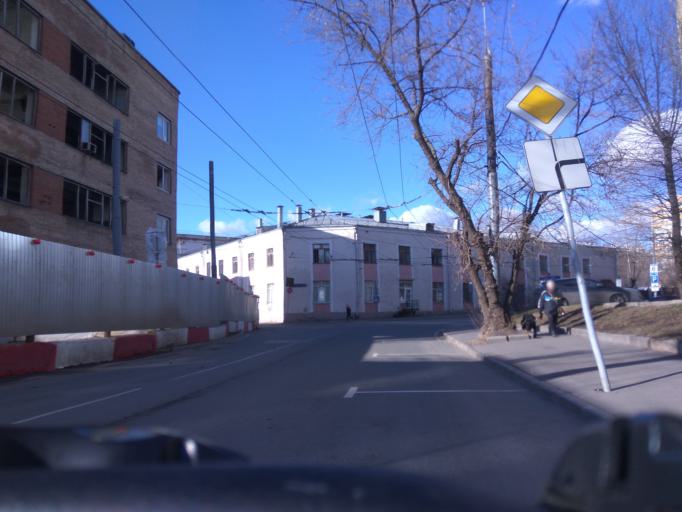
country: RU
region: Moscow
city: Mar'ina Roshcha
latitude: 55.8127
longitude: 37.6318
